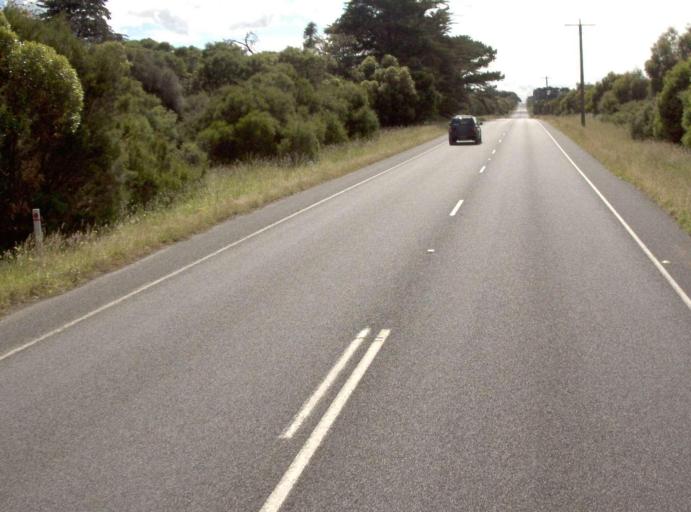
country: AU
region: Victoria
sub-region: Bass Coast
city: Phillip Island
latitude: -38.4967
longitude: 145.2127
